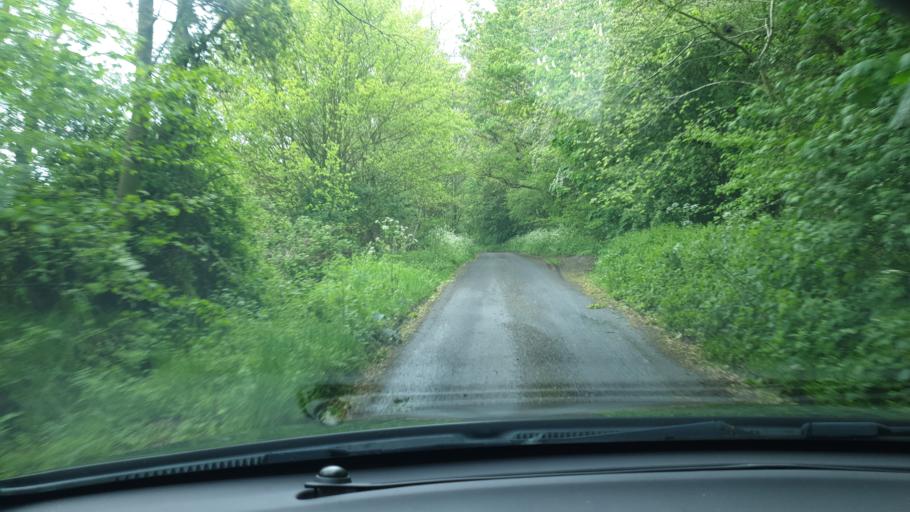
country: GB
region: England
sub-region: Essex
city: Dovercourt
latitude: 51.9121
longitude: 1.1994
